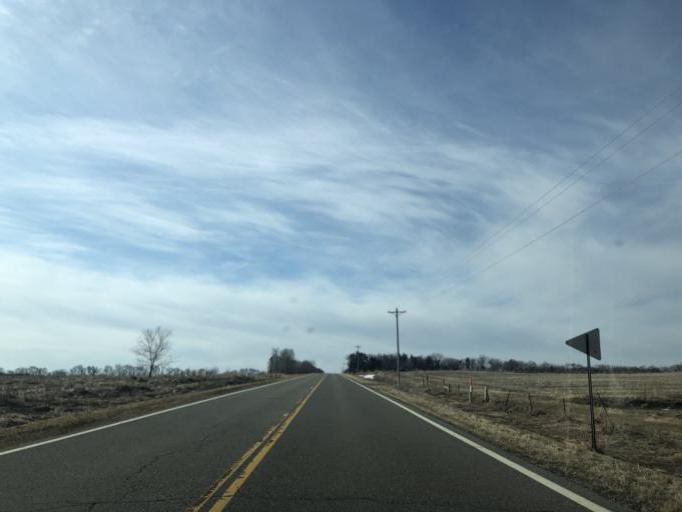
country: US
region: Minnesota
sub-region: Sherburne County
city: Becker
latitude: 45.4212
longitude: -93.8502
